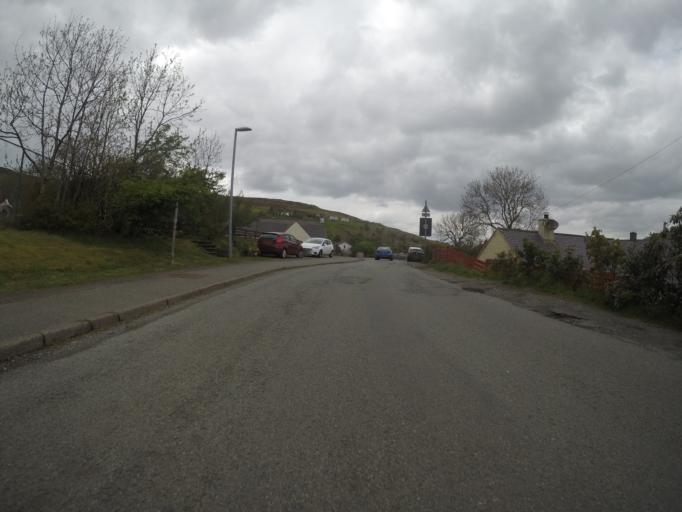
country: GB
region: Scotland
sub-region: Highland
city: Isle of Skye
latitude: 57.3022
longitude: -6.3530
